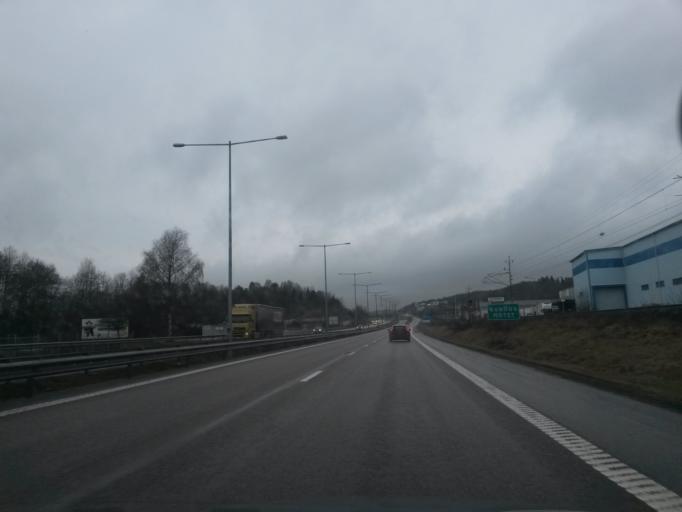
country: SE
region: Vaestra Goetaland
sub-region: Uddevalla Kommun
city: Uddevalla
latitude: 58.3525
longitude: 11.9727
